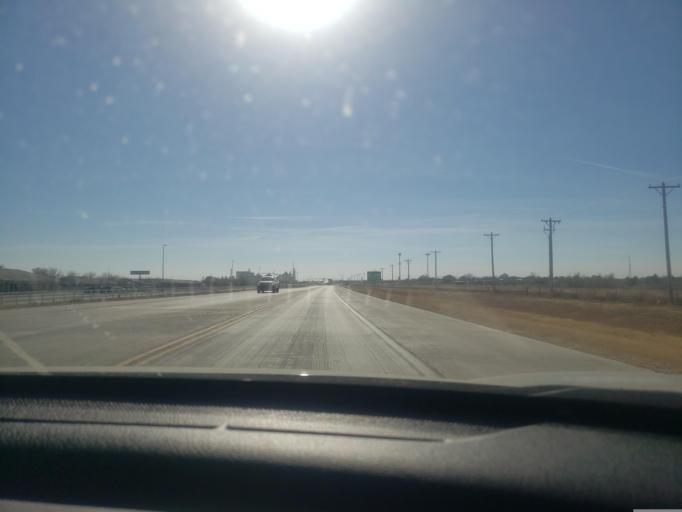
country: US
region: Kansas
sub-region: Finney County
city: Garden City
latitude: 37.9728
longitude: -100.8387
